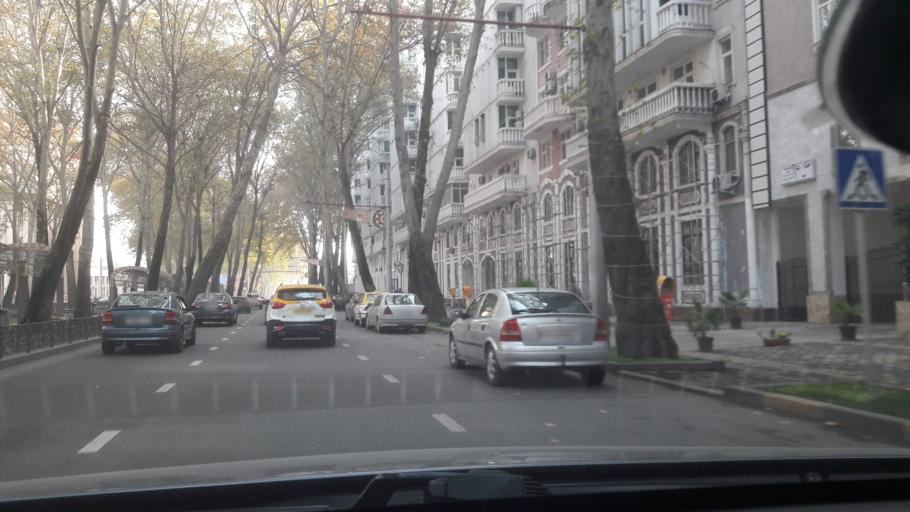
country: TJ
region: Dushanbe
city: Dushanbe
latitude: 38.5728
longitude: 68.7876
